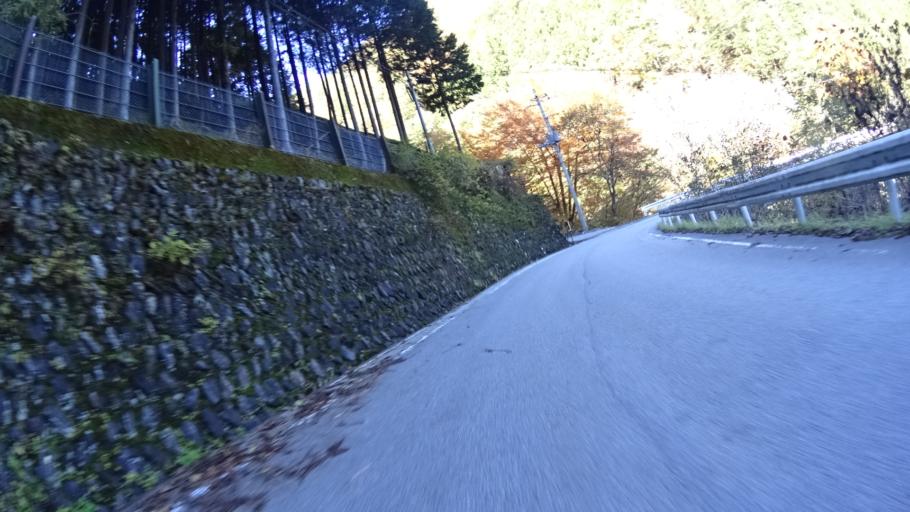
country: JP
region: Yamanashi
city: Otsuki
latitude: 35.7797
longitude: 138.9179
